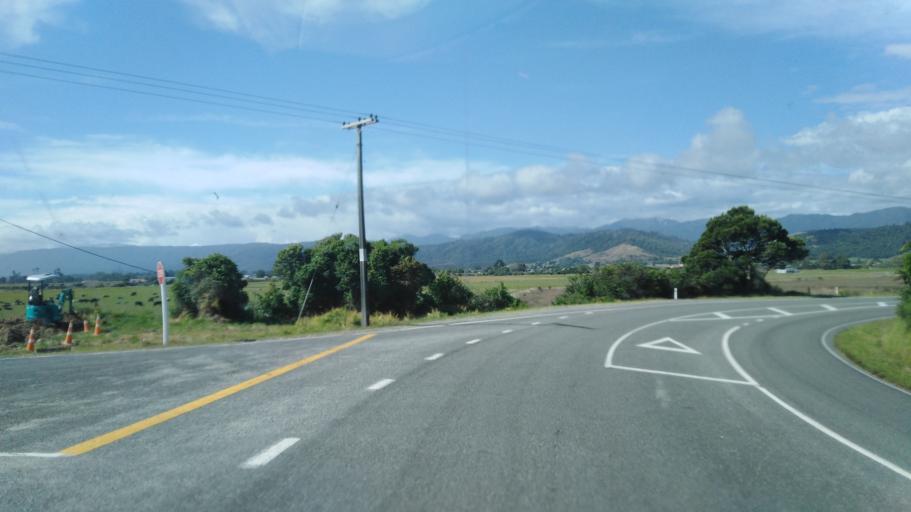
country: NZ
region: West Coast
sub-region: Buller District
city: Westport
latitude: -41.2568
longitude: 172.1133
